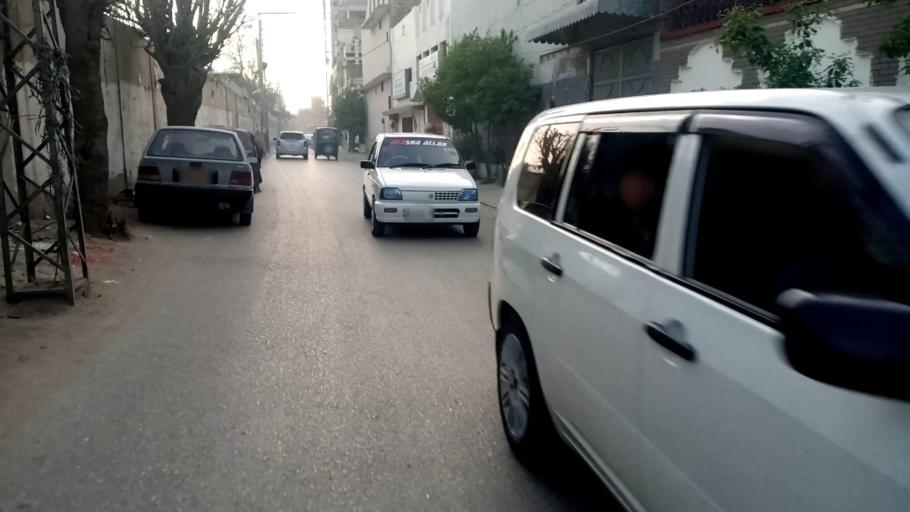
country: PK
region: Khyber Pakhtunkhwa
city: Peshawar
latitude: 34.0218
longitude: 71.5746
